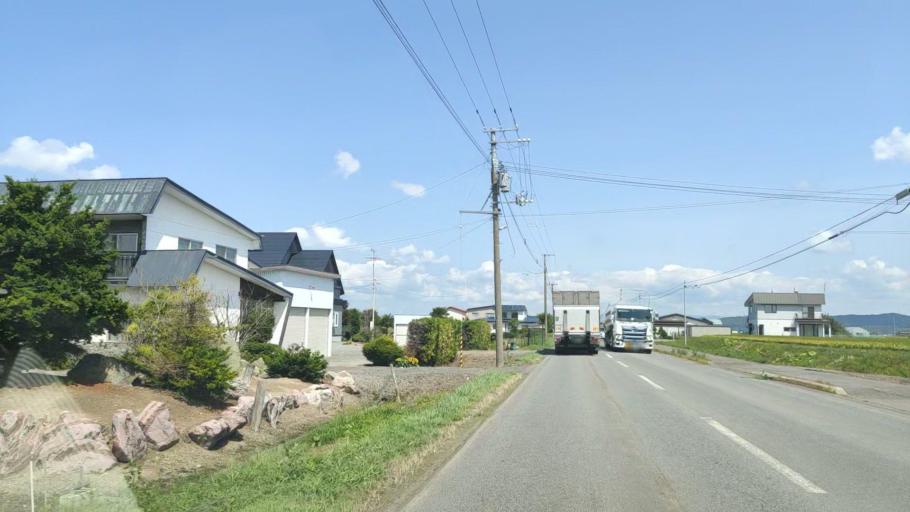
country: JP
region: Hokkaido
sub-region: Asahikawa-shi
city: Asahikawa
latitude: 43.7199
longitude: 142.4577
